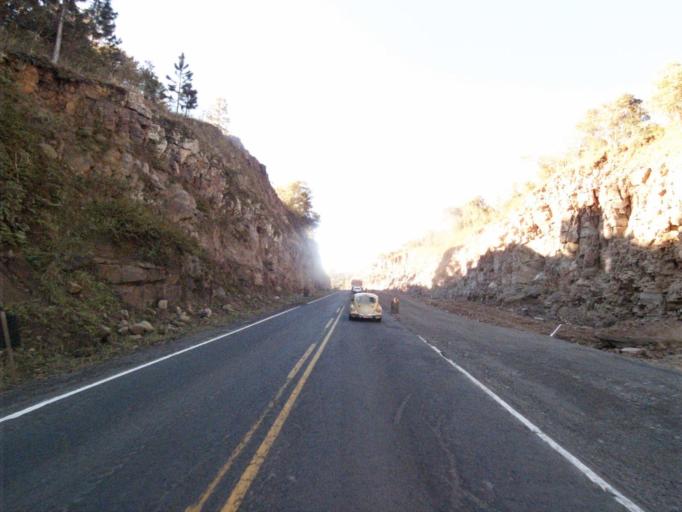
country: AR
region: Misiones
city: Bernardo de Irigoyen
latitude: -26.5746
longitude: -53.5121
